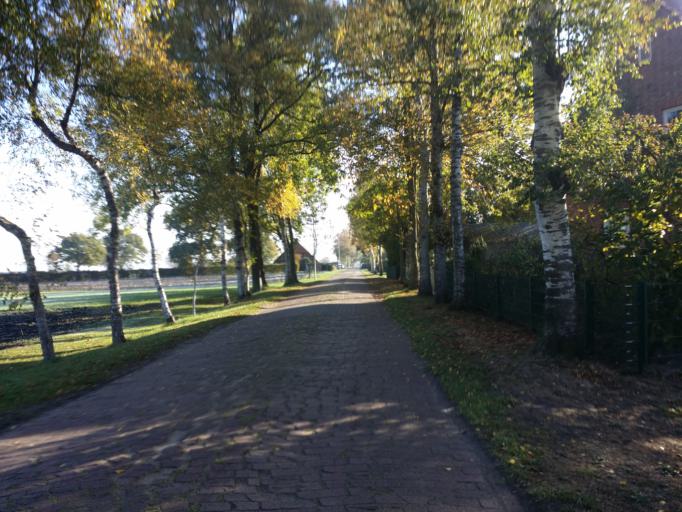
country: DE
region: Lower Saxony
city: Grasberg
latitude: 53.1918
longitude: 9.0254
